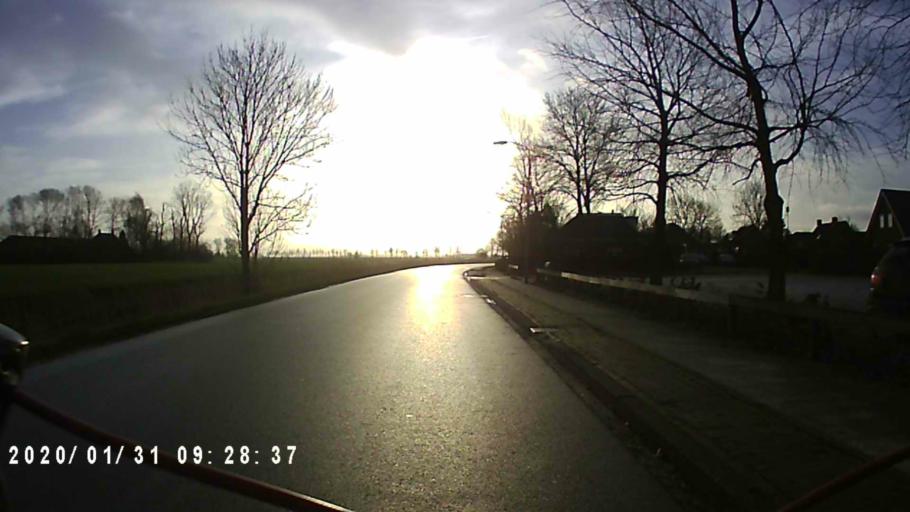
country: NL
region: Groningen
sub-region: Gemeente Zuidhorn
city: Oldehove
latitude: 53.3069
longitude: 6.4448
